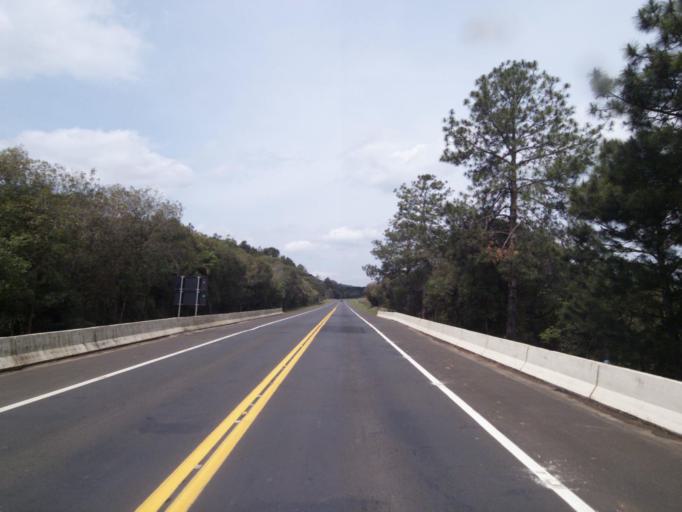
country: BR
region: Parana
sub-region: Irati
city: Irati
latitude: -25.4535
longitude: -50.4457
